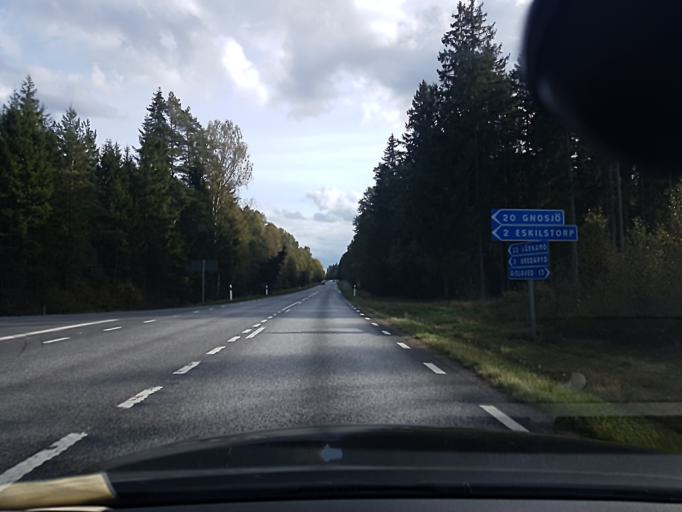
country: SE
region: Joenkoeping
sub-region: Varnamo Kommun
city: Bredaryd
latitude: 57.1966
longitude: 13.7172
